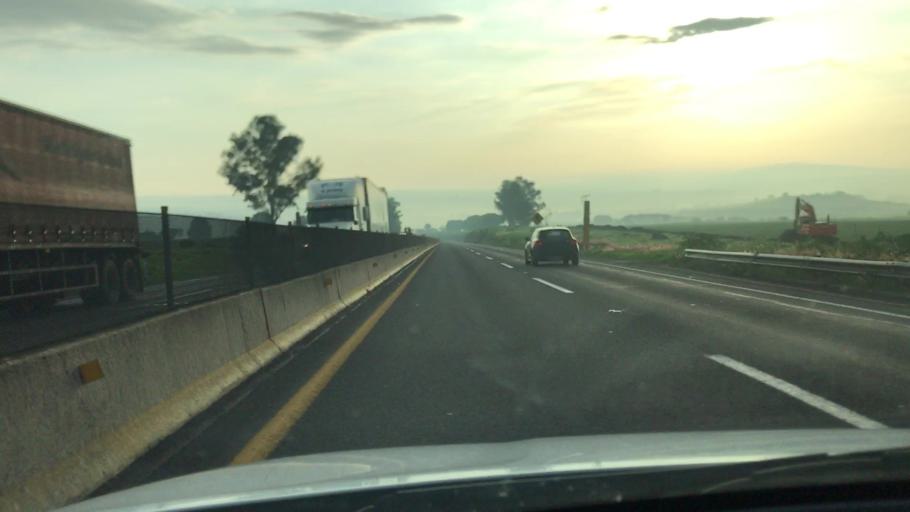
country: MX
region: Jalisco
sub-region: Acatic
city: Tierras Coloradas
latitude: 20.7783
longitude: -102.8337
